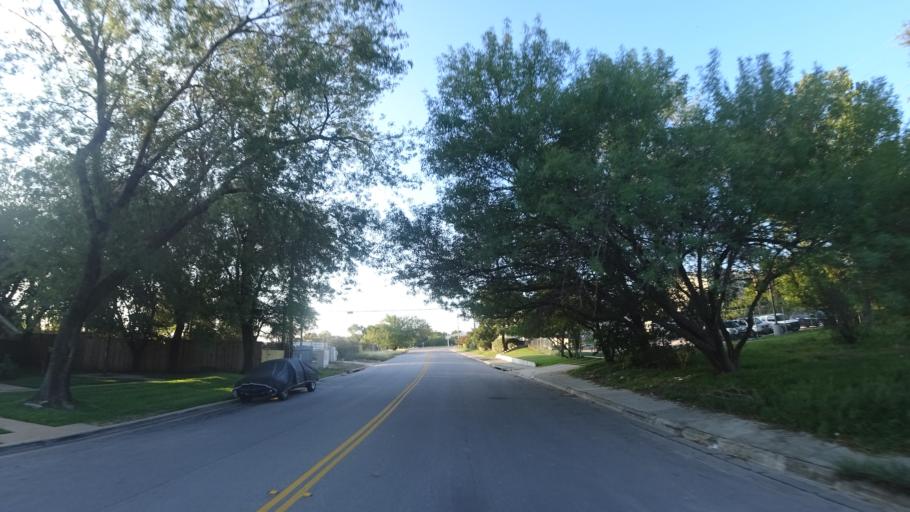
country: US
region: Texas
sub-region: Travis County
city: Austin
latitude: 30.3233
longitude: -97.6846
